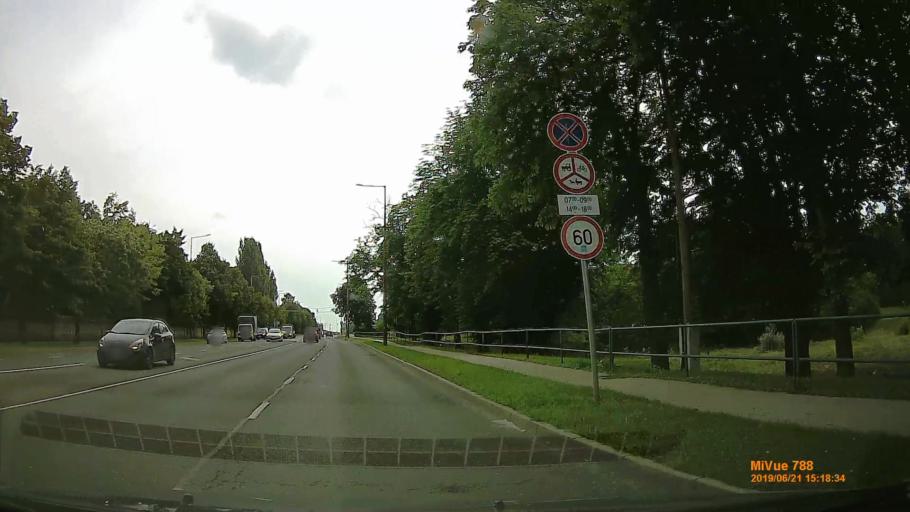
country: HU
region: Baranya
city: Pecs
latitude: 46.0491
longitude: 18.2314
